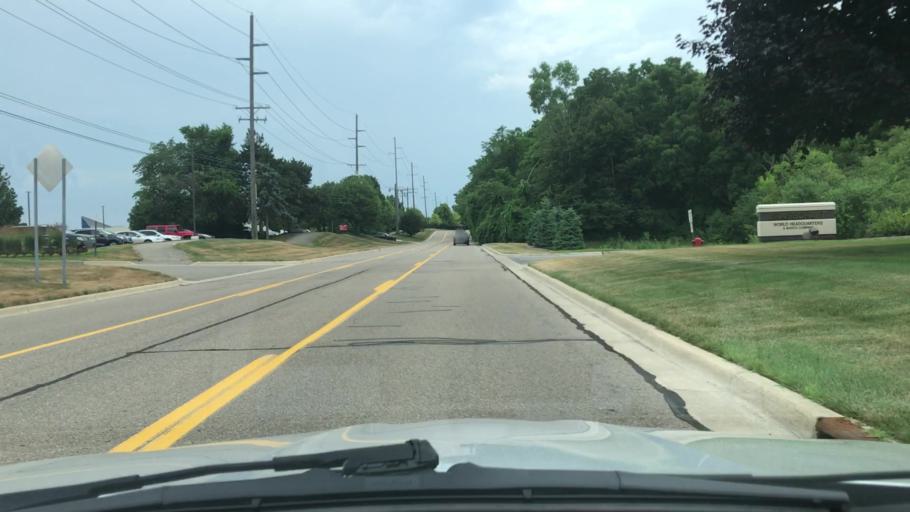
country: US
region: Michigan
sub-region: Wayne County
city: Northville
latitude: 42.4435
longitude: -83.4387
